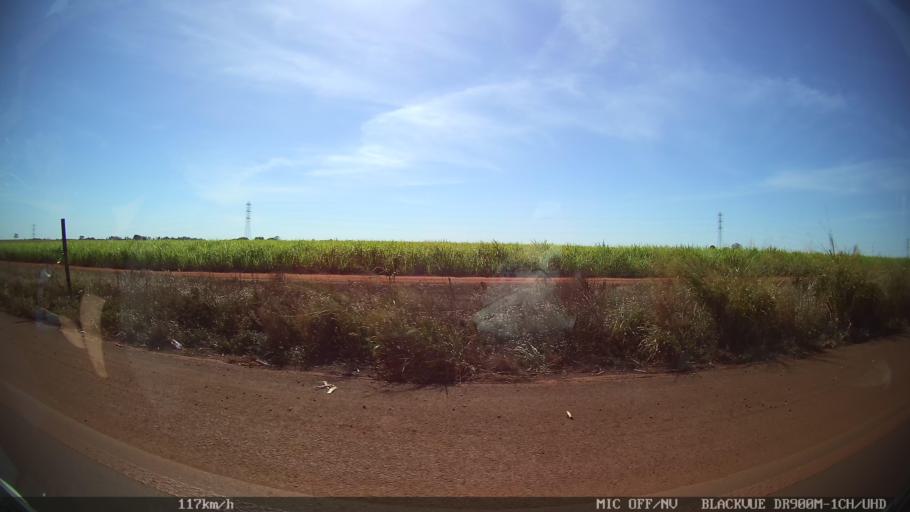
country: BR
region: Sao Paulo
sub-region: Guaira
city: Guaira
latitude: -20.4462
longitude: -48.4256
